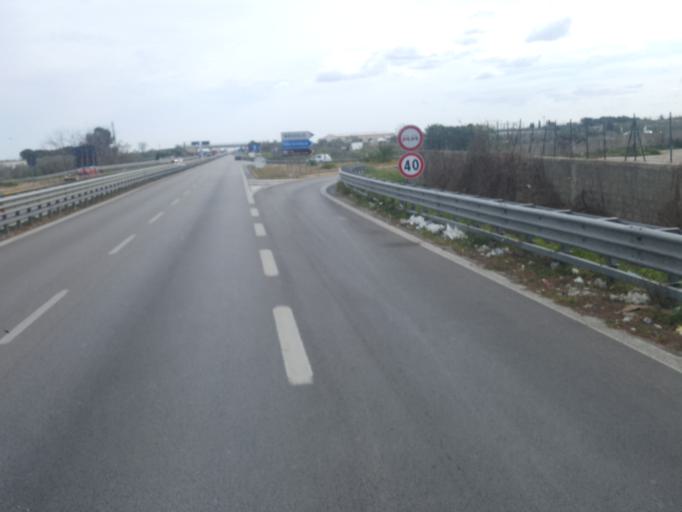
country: IT
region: Apulia
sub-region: Provincia di Barletta - Andria - Trani
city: Bisceglie
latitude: 41.2229
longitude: 16.5058
